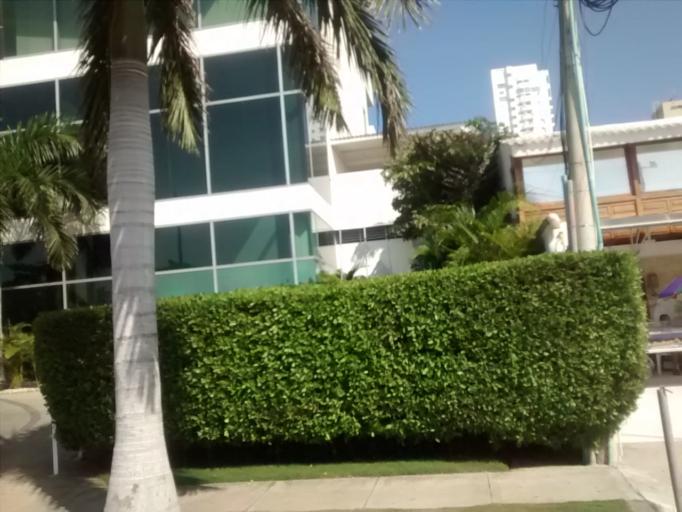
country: CO
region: Bolivar
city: Cartagena
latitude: 10.3923
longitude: -75.5468
